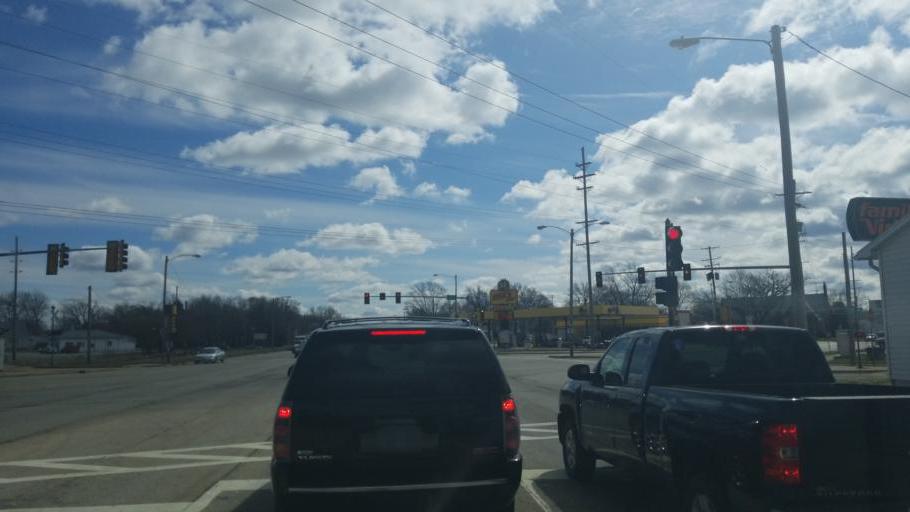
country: US
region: Illinois
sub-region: Macon County
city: Decatur
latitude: 39.8448
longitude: -88.9267
